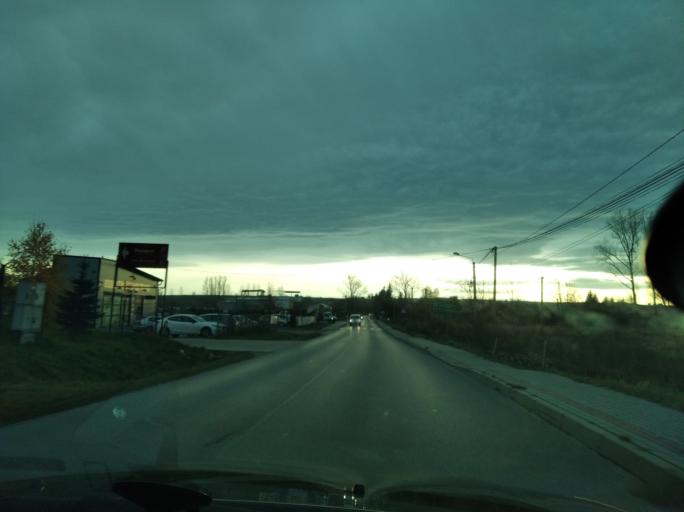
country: PL
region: Subcarpathian Voivodeship
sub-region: Powiat rzeszowski
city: Niechobrz
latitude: 50.0216
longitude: 21.8823
